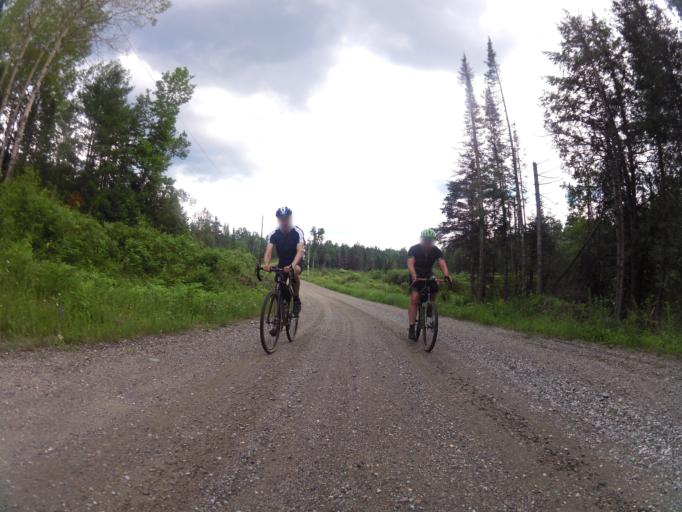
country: CA
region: Ontario
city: Renfrew
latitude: 45.0624
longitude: -76.7551
